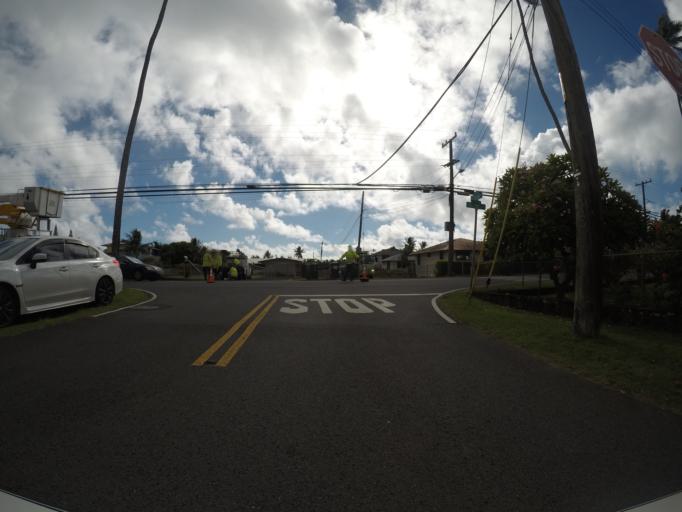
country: US
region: Hawaii
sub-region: Honolulu County
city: Kailua
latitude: 21.4017
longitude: -157.7443
